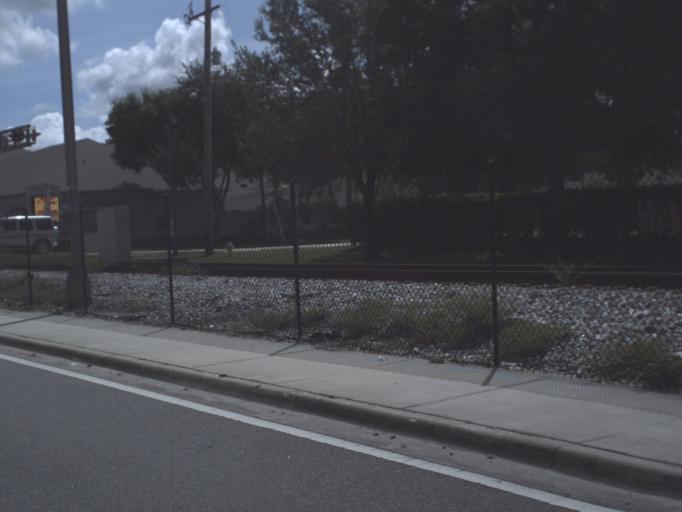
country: US
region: Florida
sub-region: Hillsborough County
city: Carrollwood
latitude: 28.0359
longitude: -82.4929
